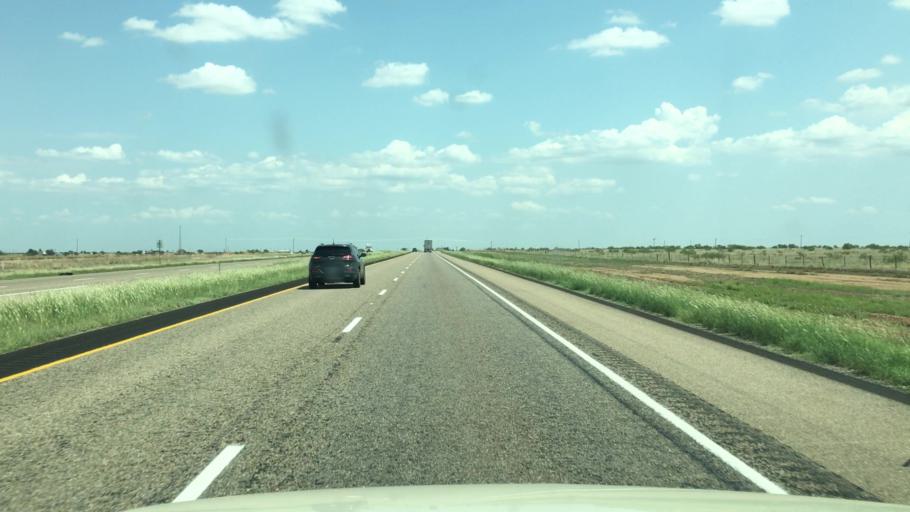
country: US
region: Texas
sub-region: Armstrong County
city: Claude
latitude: 35.0361
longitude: -101.2018
